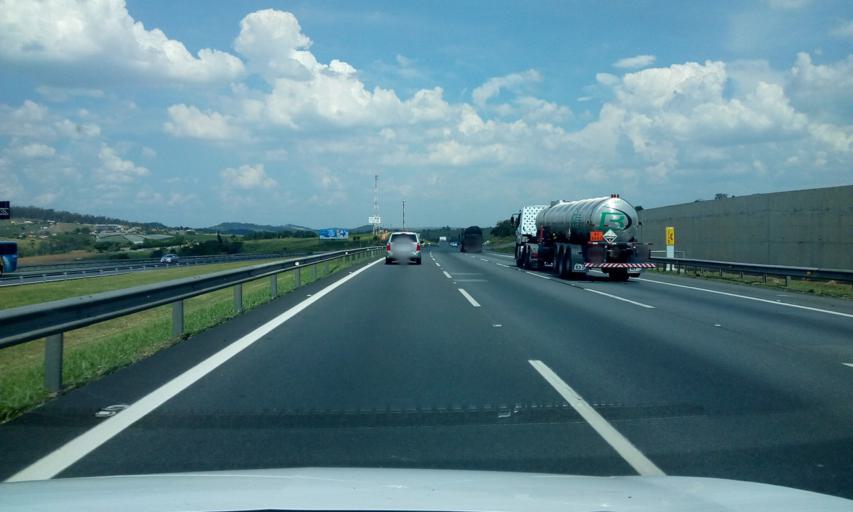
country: BR
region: Sao Paulo
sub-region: Valinhos
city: Valinhos
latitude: -23.0156
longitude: -47.0838
